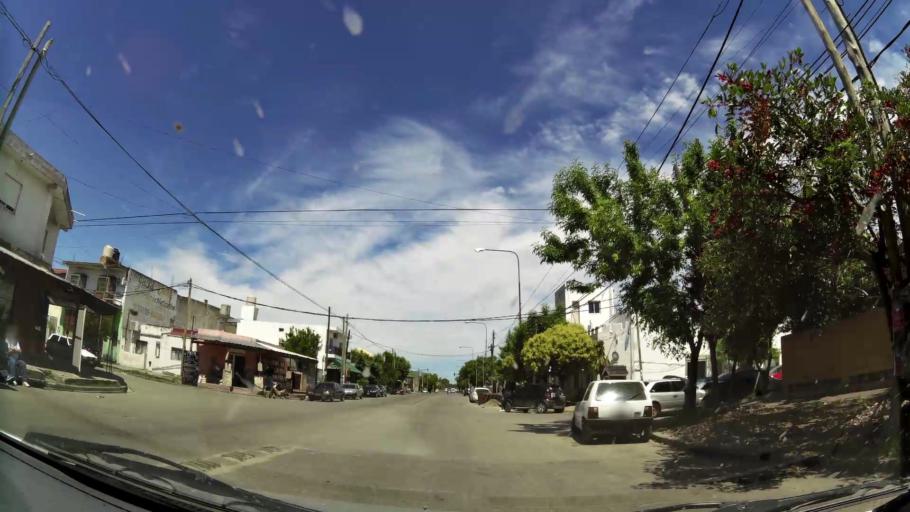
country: AR
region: Buenos Aires
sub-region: Partido de Quilmes
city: Quilmes
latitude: -34.7316
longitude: -58.3032
